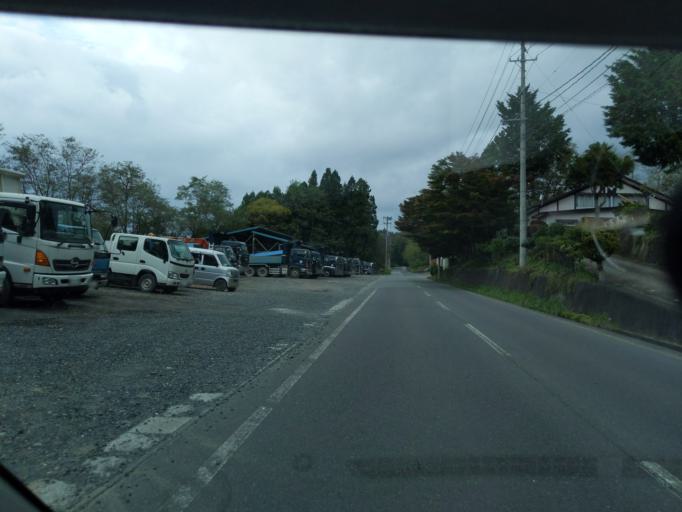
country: JP
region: Iwate
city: Mizusawa
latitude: 39.0481
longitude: 141.1140
